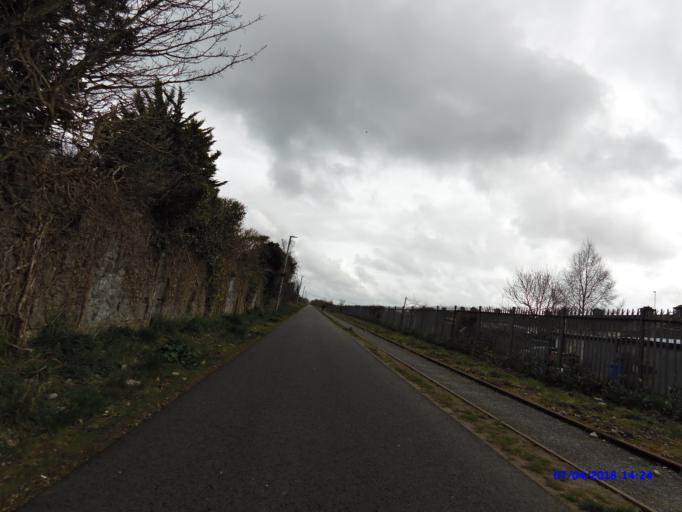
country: IE
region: Leinster
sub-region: An Iarmhi
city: Athlone
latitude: 53.4276
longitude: -7.9292
